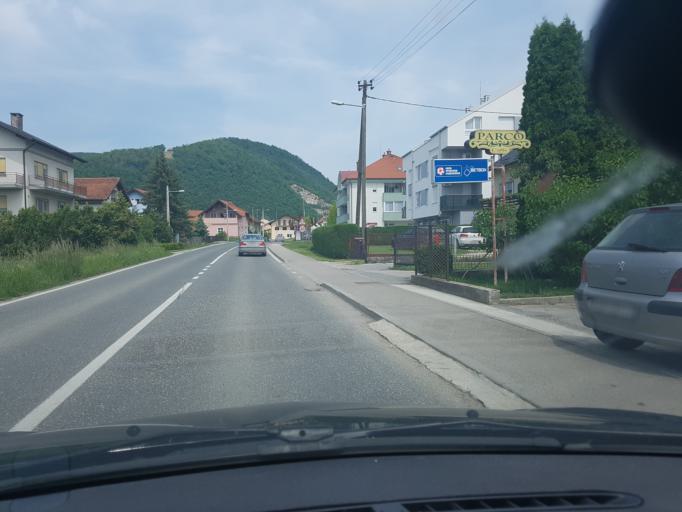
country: HR
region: Krapinsko-Zagorska
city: Pregrada
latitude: 46.1582
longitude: 15.7552
